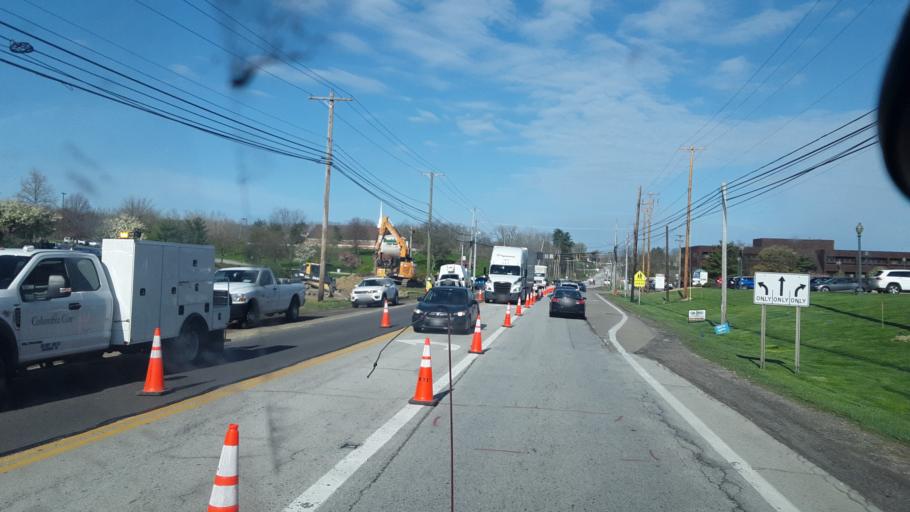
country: US
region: Ohio
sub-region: Medina County
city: Medina
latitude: 41.1365
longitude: -81.8156
